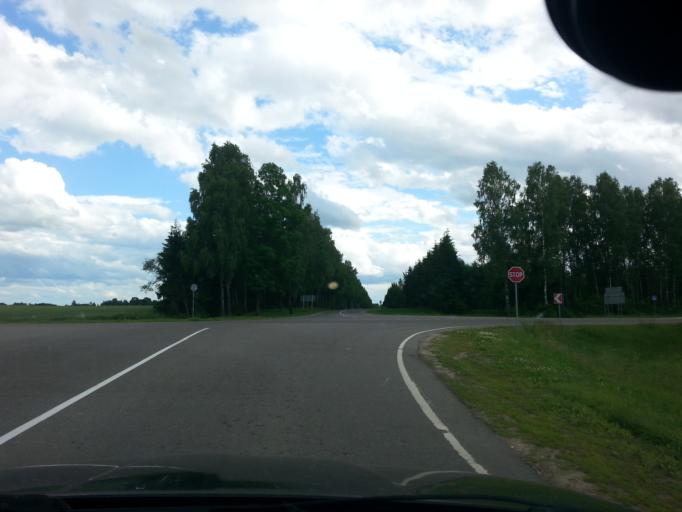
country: BY
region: Minsk
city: Svir
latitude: 54.8922
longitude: 26.3886
